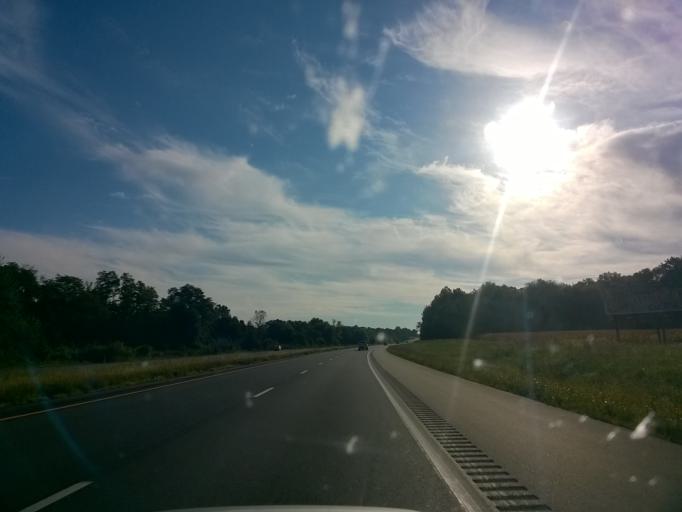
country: US
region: Indiana
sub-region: Gibson County
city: Oakland City
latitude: 38.1922
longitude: -87.3381
